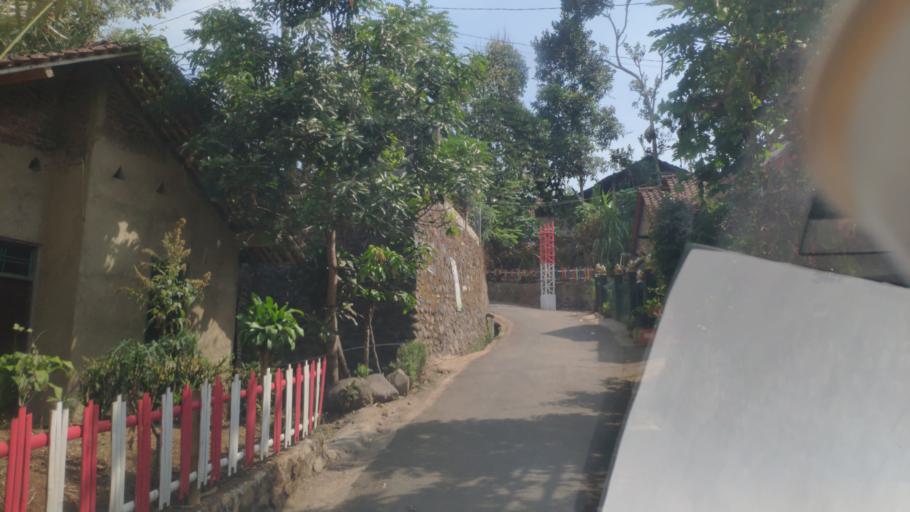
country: ID
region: Central Java
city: Wonosobo
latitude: -7.3939
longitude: 109.7299
